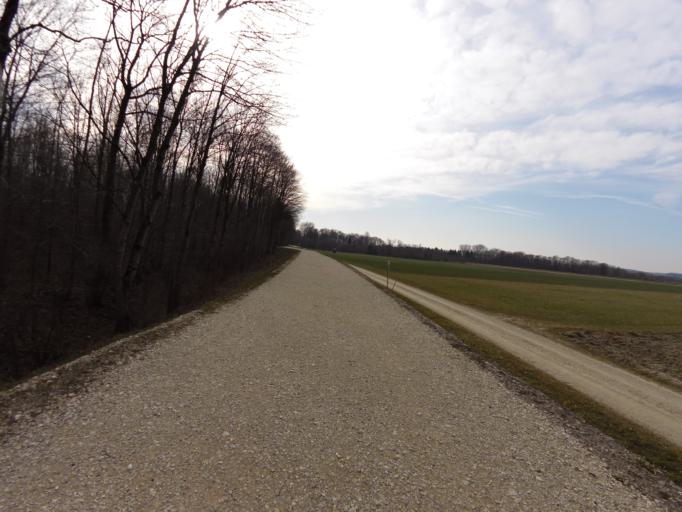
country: DE
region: Bavaria
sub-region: Lower Bavaria
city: Tiefenbach
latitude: 48.5245
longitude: 12.1120
